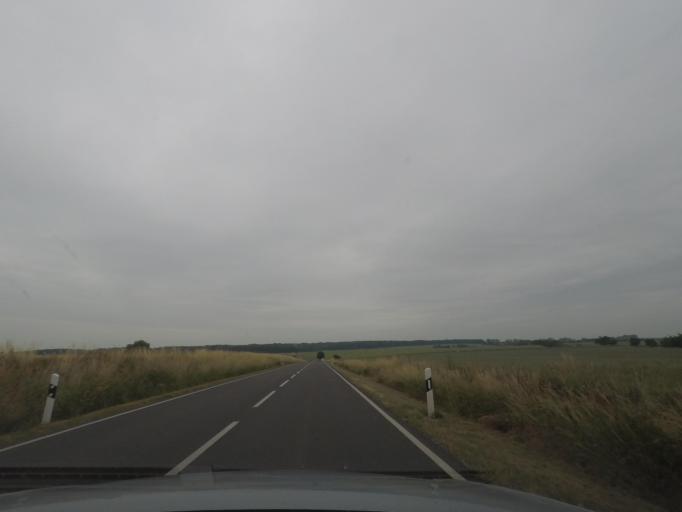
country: DE
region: Saxony-Anhalt
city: Seehausen
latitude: 52.0904
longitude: 11.2873
